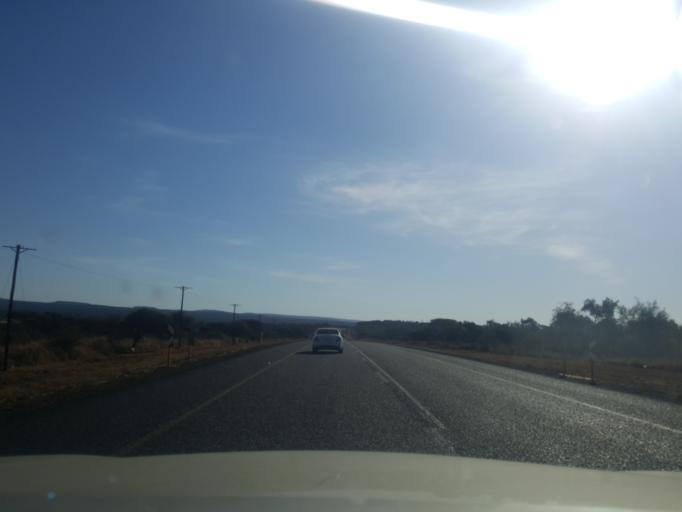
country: ZA
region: North-West
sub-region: Ngaka Modiri Molema District Municipality
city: Zeerust
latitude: -25.5387
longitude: 26.0388
